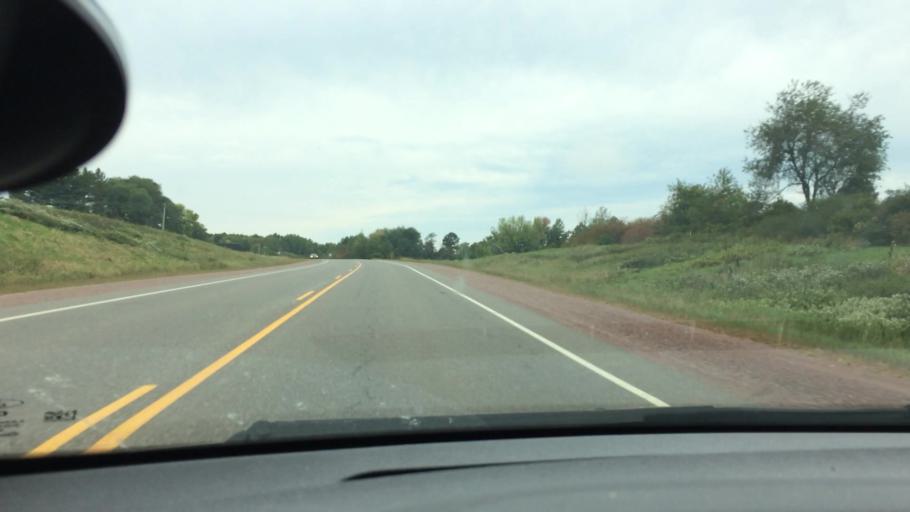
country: US
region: Wisconsin
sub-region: Clark County
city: Neillsville
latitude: 44.5522
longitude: -90.6160
